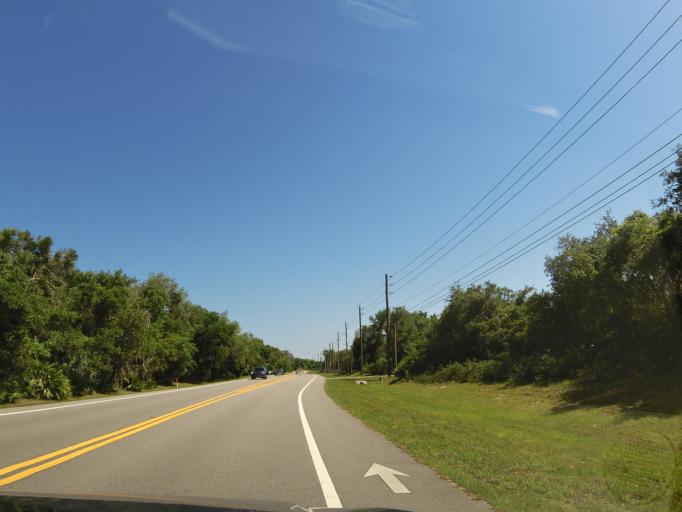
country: US
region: Florida
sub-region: Flagler County
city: Flagler Beach
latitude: 29.4293
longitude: -81.1530
